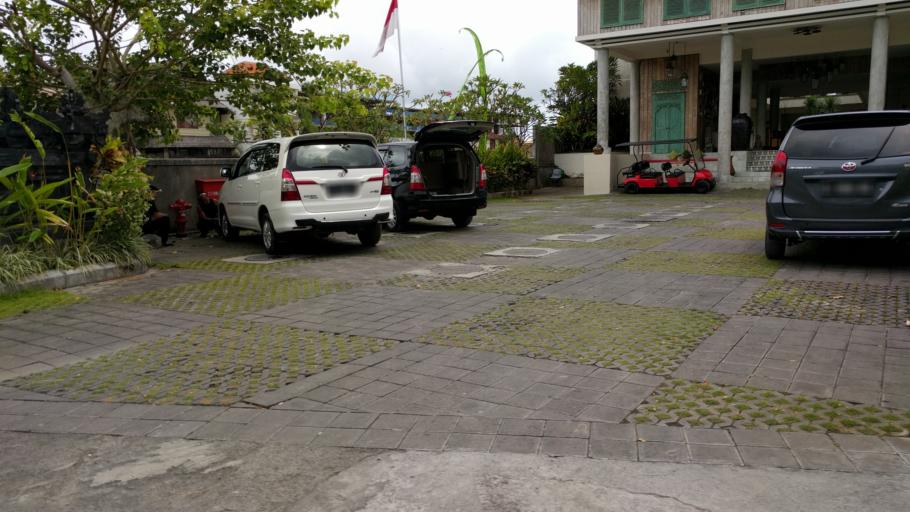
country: ID
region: Bali
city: Kuta
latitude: -8.6750
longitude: 115.1529
